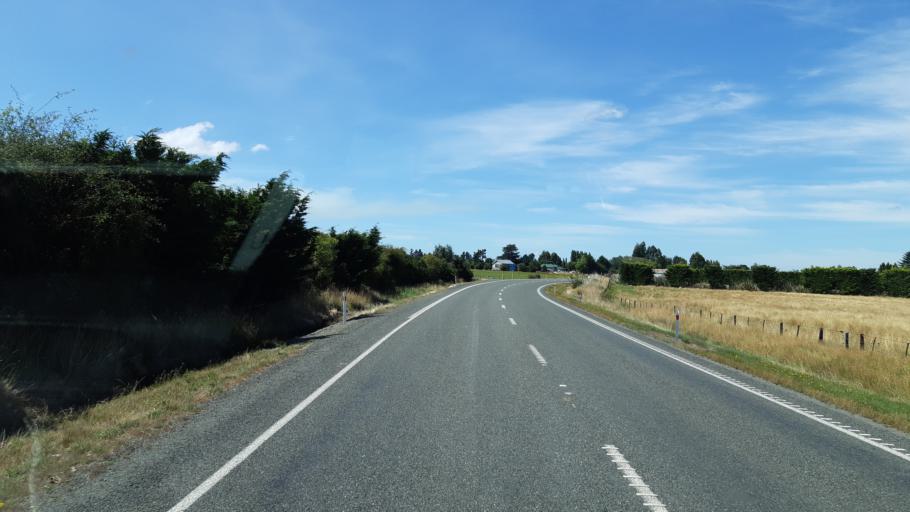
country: NZ
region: Southland
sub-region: Southland District
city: Winton
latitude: -45.8343
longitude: 168.5820
